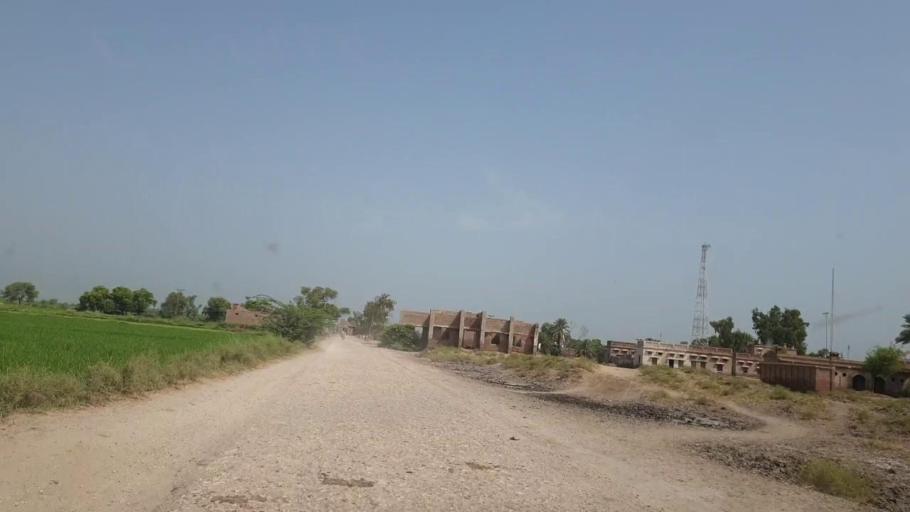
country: PK
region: Sindh
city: Lakhi
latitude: 27.8700
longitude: 68.6607
